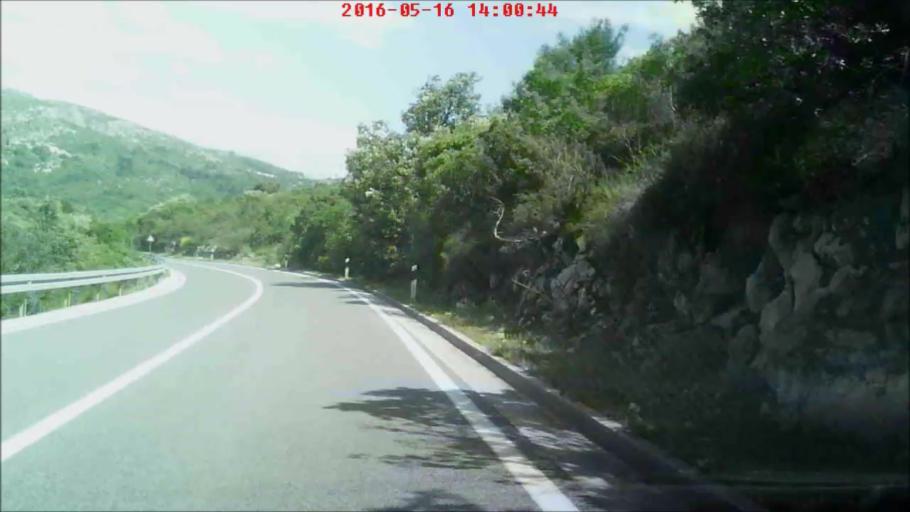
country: HR
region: Dubrovacko-Neretvanska
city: Ston
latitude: 42.8318
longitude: 17.7416
